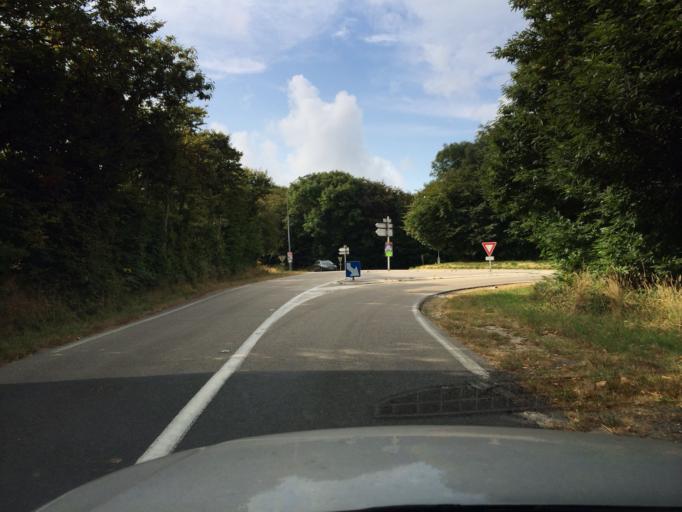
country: FR
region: Lower Normandy
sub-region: Departement de la Manche
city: Beaumont-Hague
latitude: 49.6732
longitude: -1.8564
